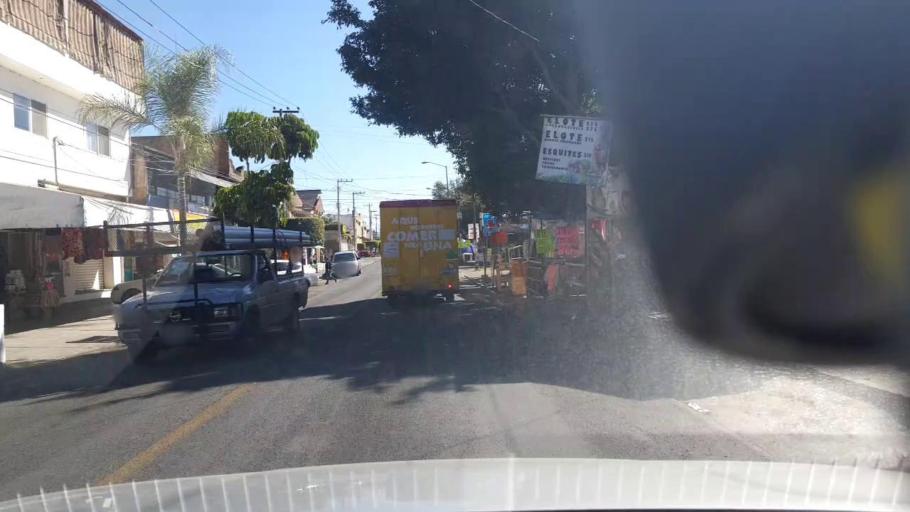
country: MX
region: Morelos
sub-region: Cuernavaca
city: Lomas de Ahuatepec
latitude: 18.9695
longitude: -99.2220
